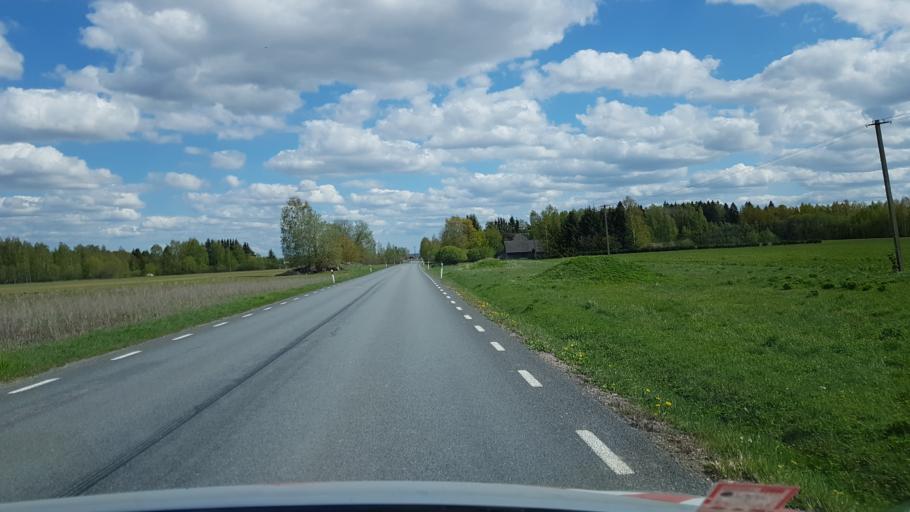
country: EE
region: Tartu
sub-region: UElenurme vald
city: Ulenurme
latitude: 58.3120
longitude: 26.6608
